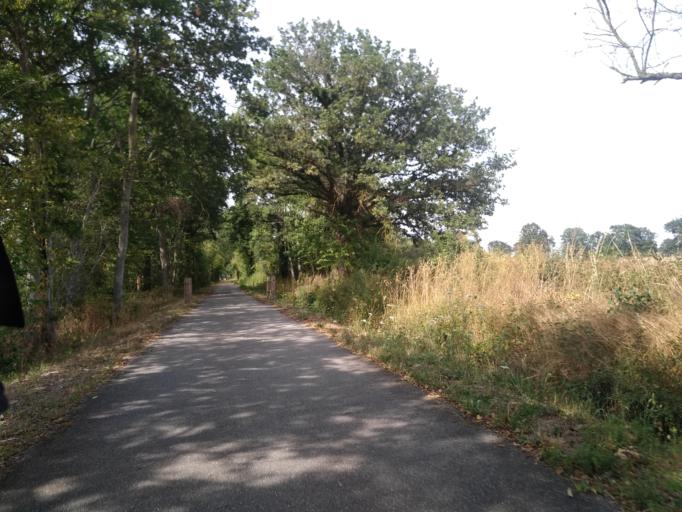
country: FR
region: Bourgogne
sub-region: Departement de Saone-et-Loire
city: Bourbon-Lancy
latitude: 46.5895
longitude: 3.7456
